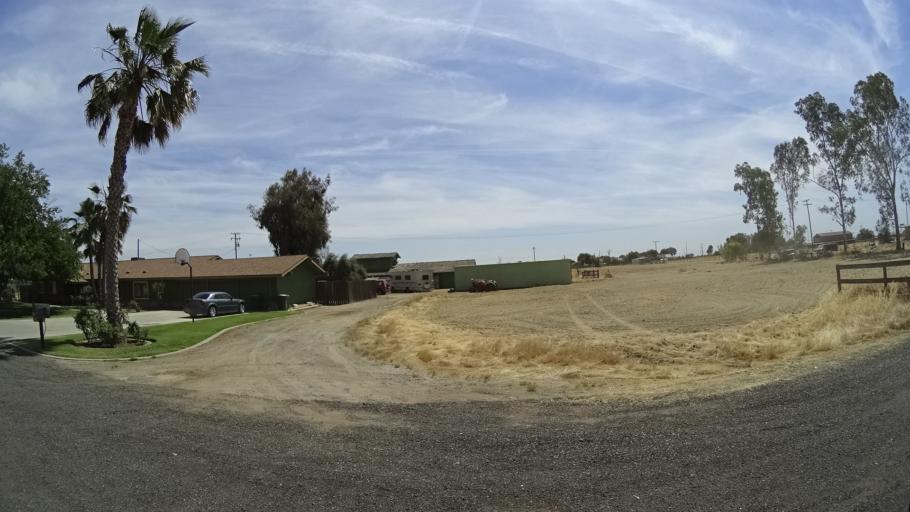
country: US
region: California
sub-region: Kings County
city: Home Garden
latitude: 36.3311
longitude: -119.5885
